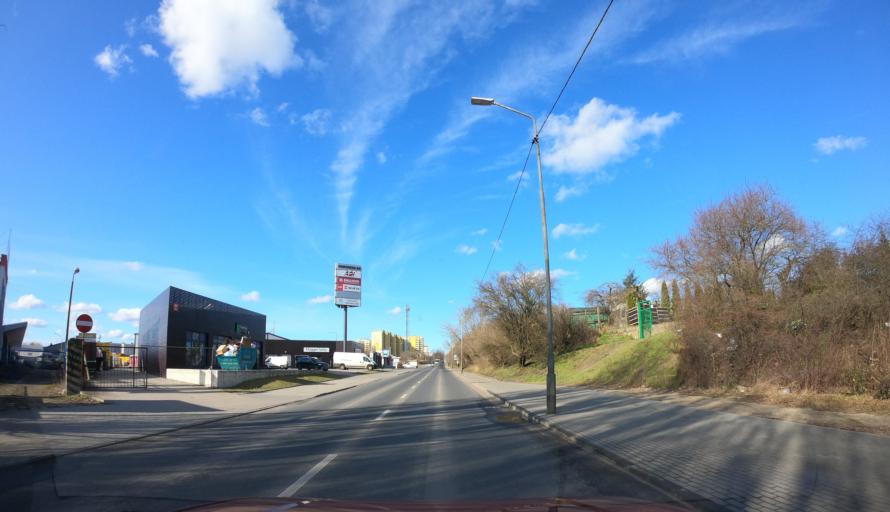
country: PL
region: West Pomeranian Voivodeship
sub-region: Szczecin
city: Szczecin
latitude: 53.4250
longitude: 14.5125
